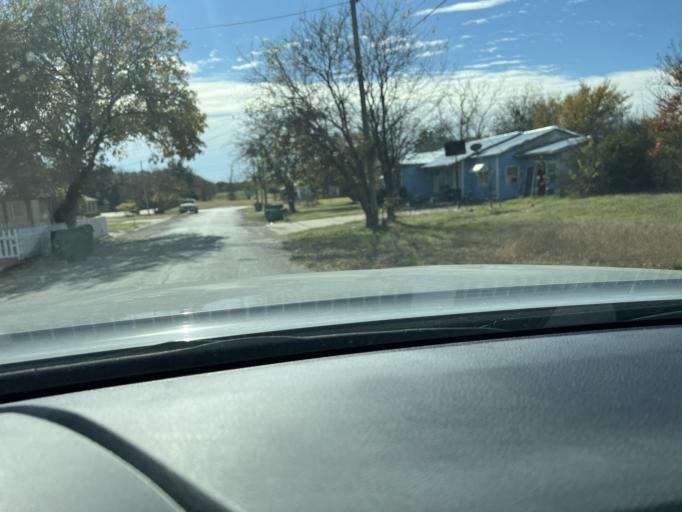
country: US
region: Texas
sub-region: Eastland County
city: Eastland
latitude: 32.3963
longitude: -98.8191
